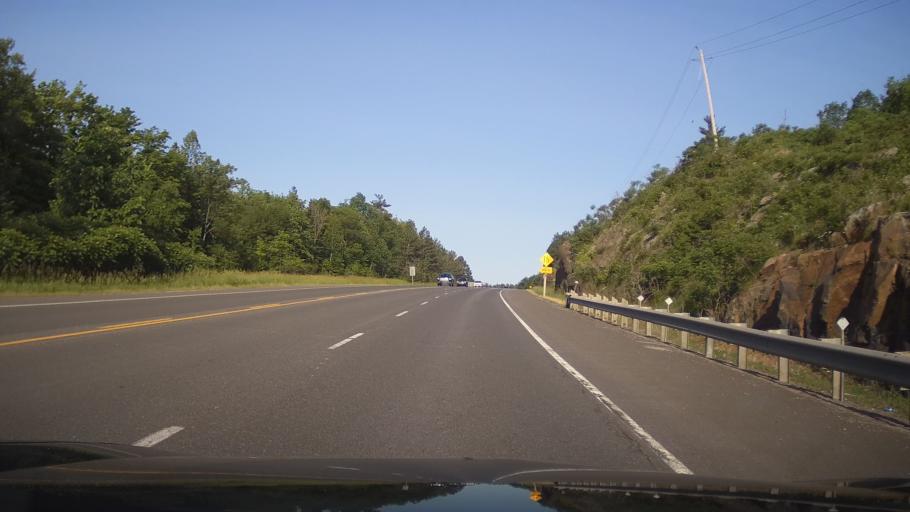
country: CA
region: Ontario
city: Quinte West
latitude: 44.5021
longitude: -77.5253
